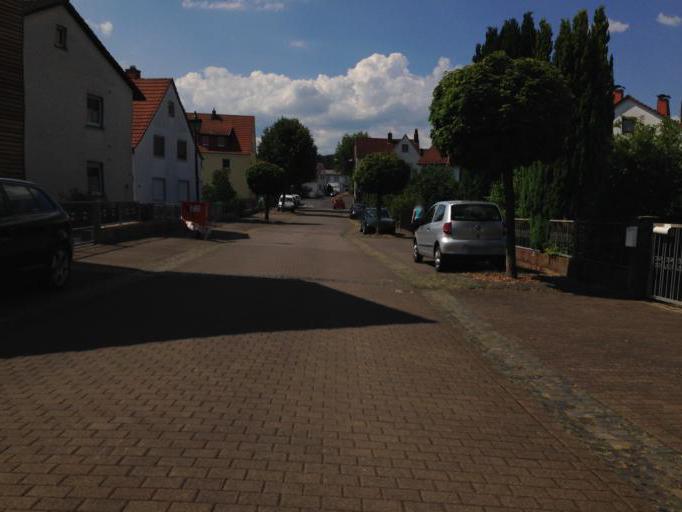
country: DE
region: Hesse
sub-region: Regierungsbezirk Giessen
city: Heuchelheim
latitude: 50.6252
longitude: 8.6320
